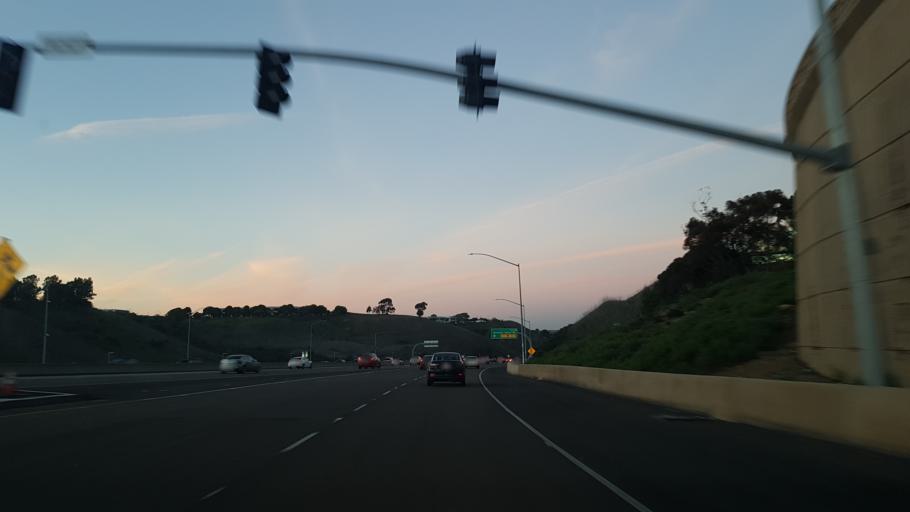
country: US
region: California
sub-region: San Diego County
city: La Jolla
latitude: 32.8898
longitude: -117.2271
